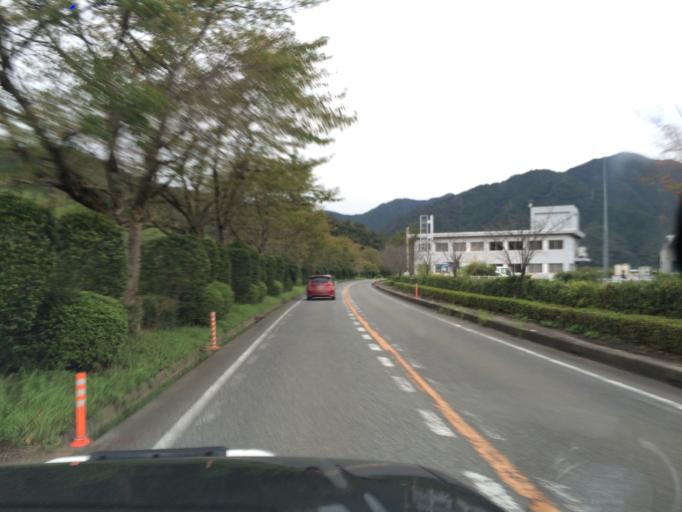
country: JP
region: Hyogo
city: Toyooka
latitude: 35.3747
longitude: 134.8139
